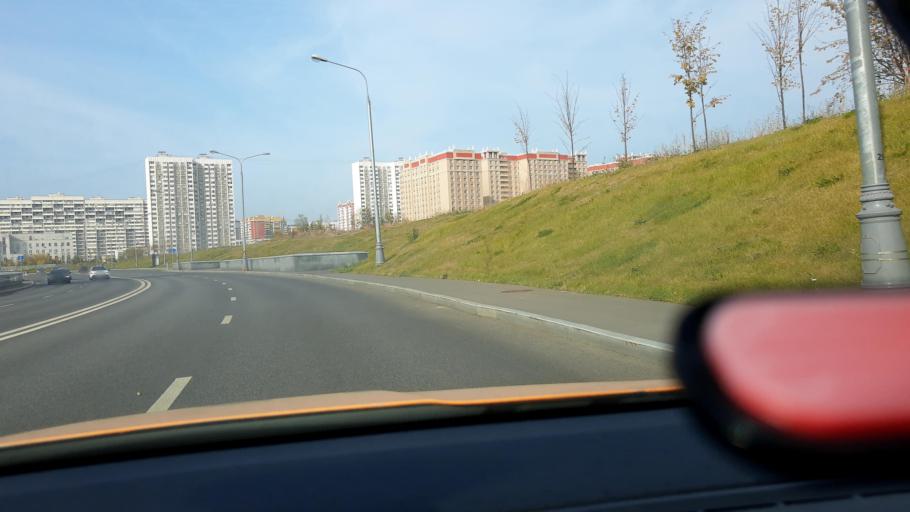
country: RU
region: Moscow
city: Ramenki
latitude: 55.6922
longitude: 37.5145
